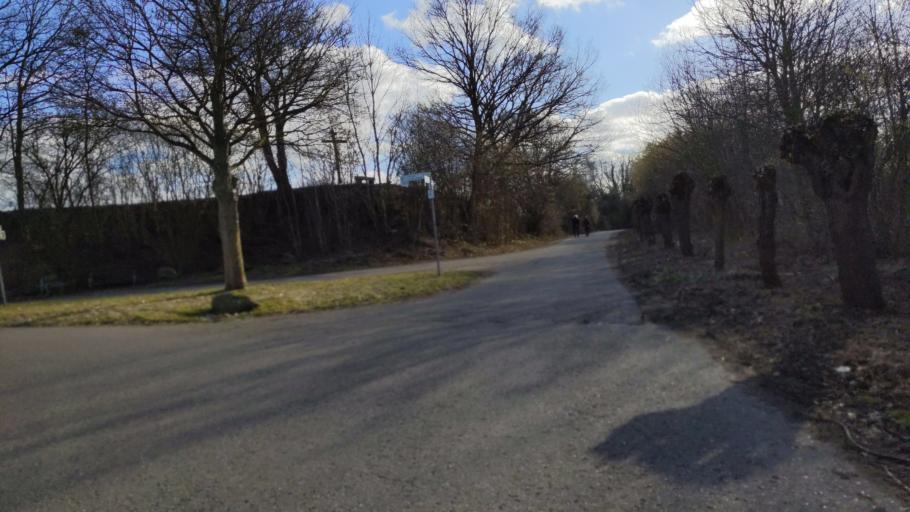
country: DE
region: Schleswig-Holstein
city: Timmendorfer Strand
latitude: 53.9956
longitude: 10.7551
